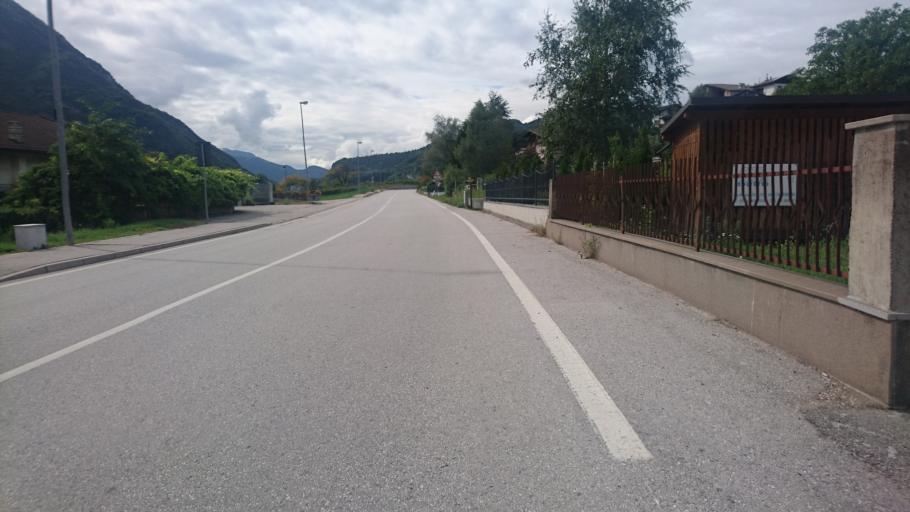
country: IT
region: Trentino-Alto Adige
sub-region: Provincia di Trento
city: Civezzano
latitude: 46.0838
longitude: 11.1978
